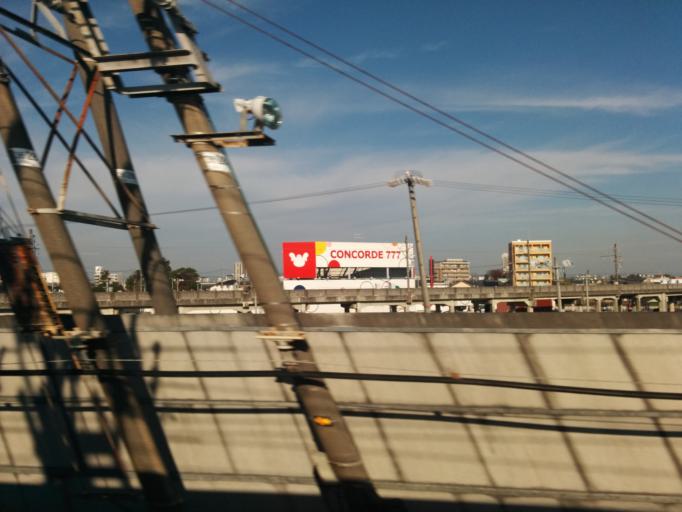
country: JP
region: Aichi
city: Sobue
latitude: 35.3128
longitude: 136.6892
